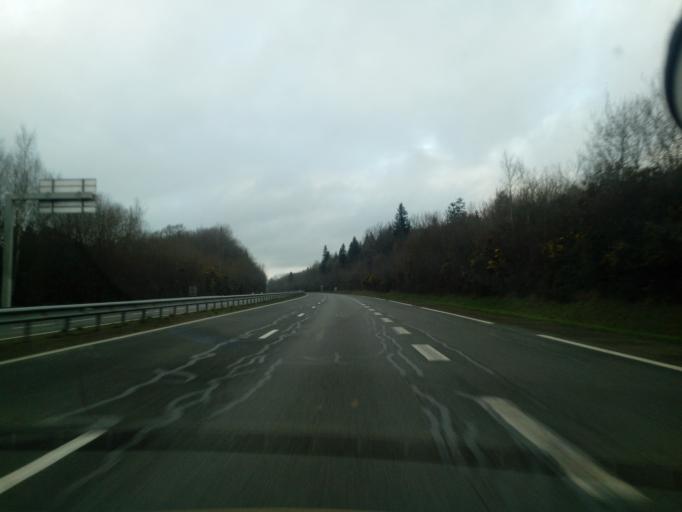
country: FR
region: Brittany
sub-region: Departement d'Ille-et-Vilaine
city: Saint-Meen-le-Grand
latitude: 48.1907
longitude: -2.2135
